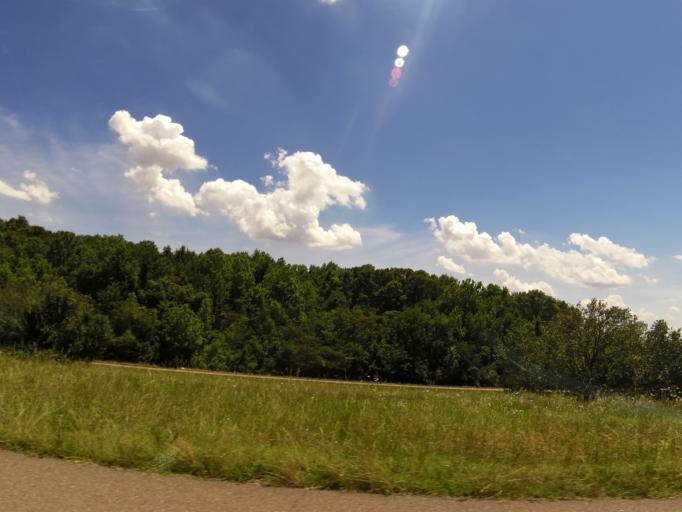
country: US
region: Tennessee
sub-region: Dyer County
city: Dyersburg
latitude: 36.0754
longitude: -89.4964
